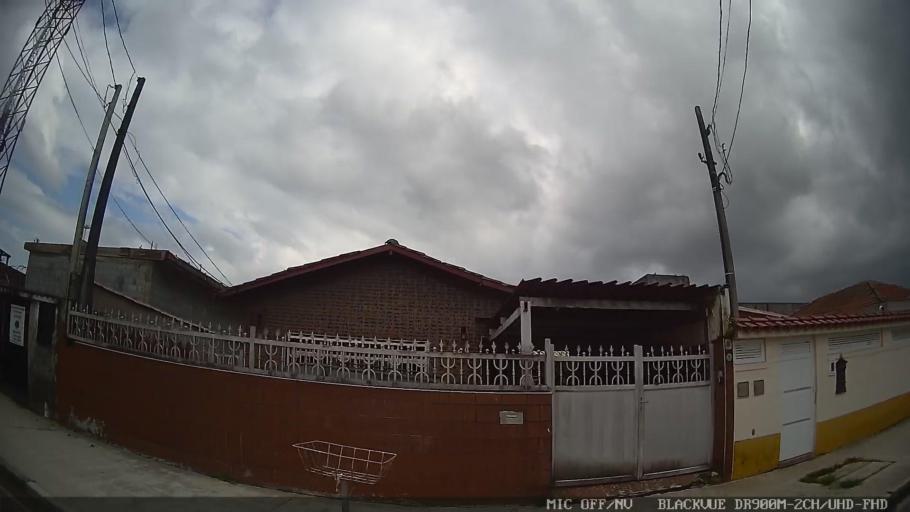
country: BR
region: Sao Paulo
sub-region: Guaruja
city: Guaruja
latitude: -23.9936
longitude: -46.2903
